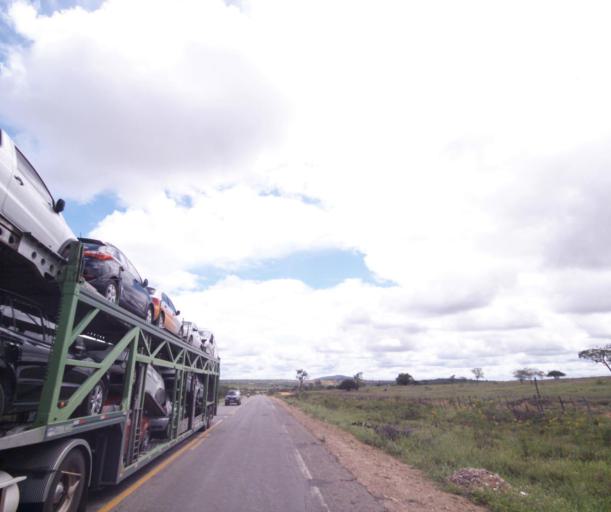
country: BR
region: Bahia
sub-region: Tanhacu
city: Tanhacu
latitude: -14.1551
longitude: -41.2023
